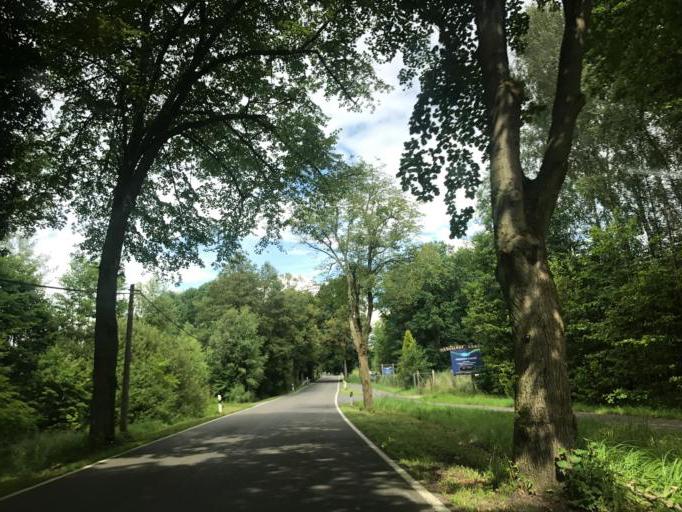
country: DE
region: Brandenburg
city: Rheinsberg
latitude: 53.1920
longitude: 12.8909
